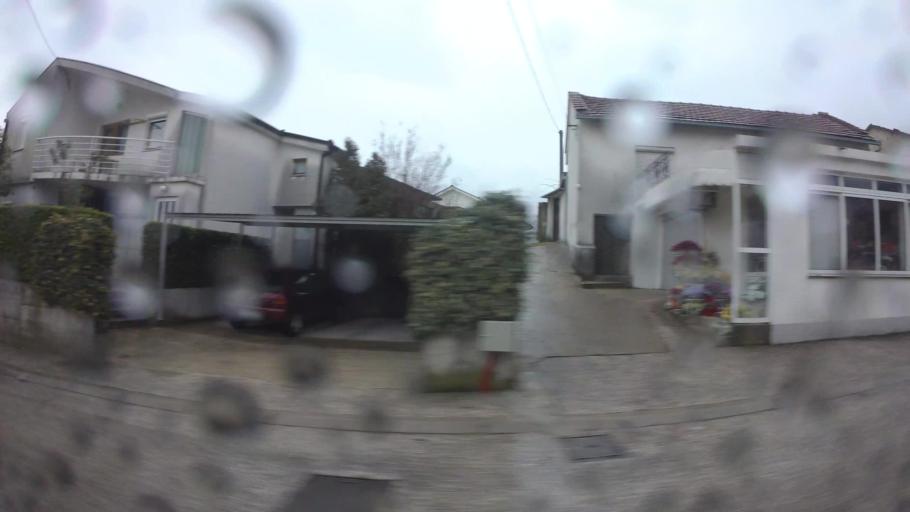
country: BA
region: Federation of Bosnia and Herzegovina
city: Cim
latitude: 43.3513
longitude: 17.7814
